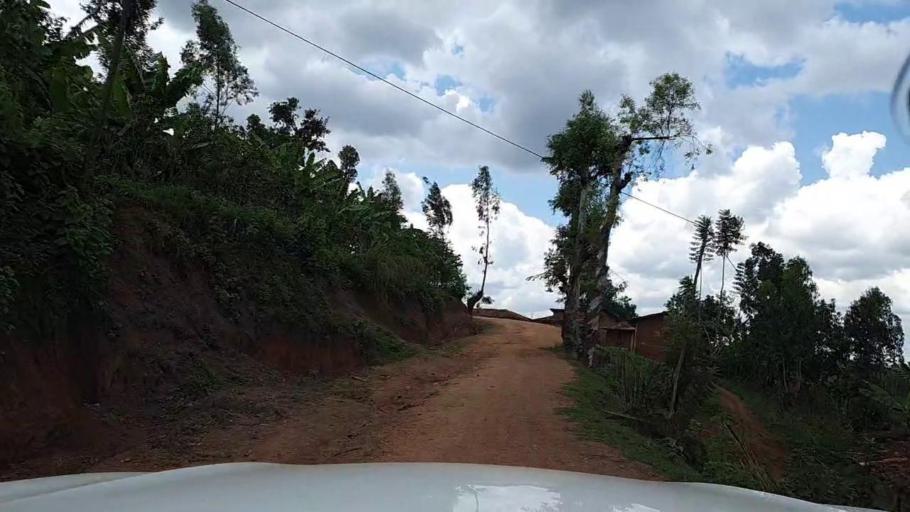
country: RW
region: Southern Province
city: Butare
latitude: -2.7521
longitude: 29.7594
